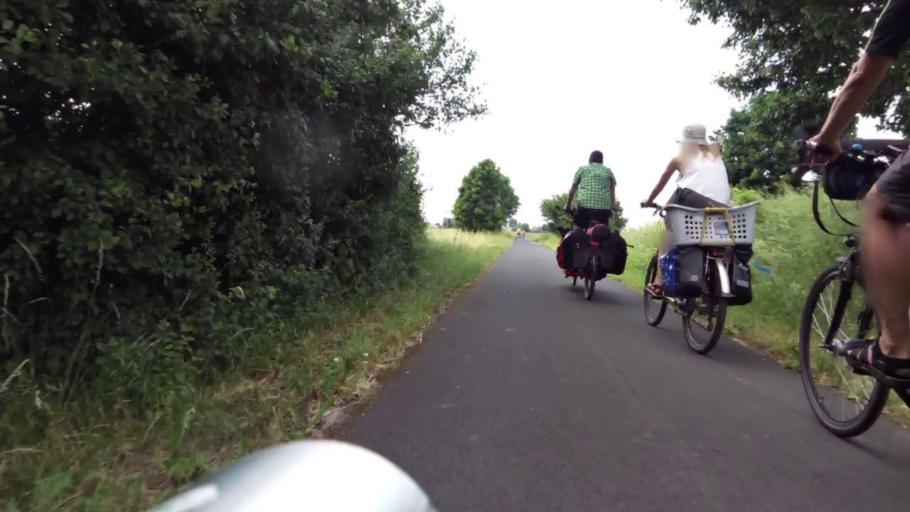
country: PL
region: Kujawsko-Pomorskie
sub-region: Powiat torunski
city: Lubianka
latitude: 53.1260
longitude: 18.4671
